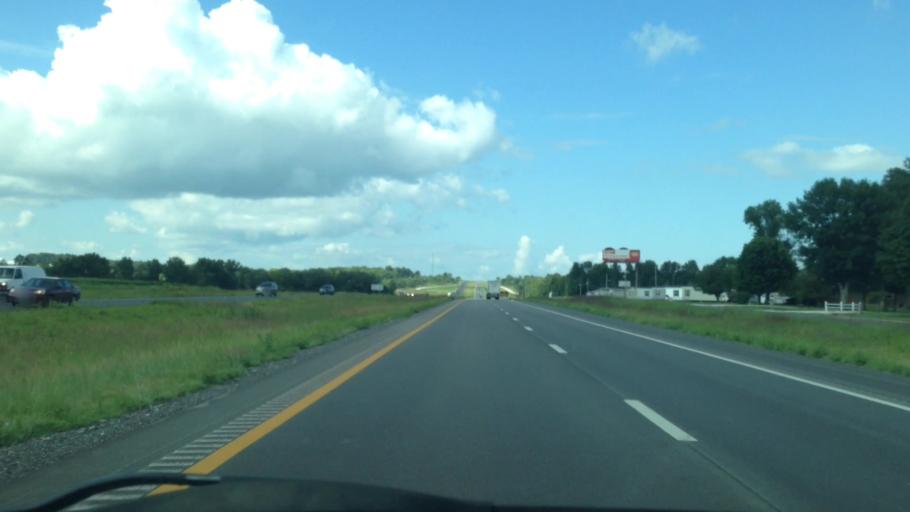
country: US
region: Illinois
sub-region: Adams County
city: Quincy
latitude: 39.9970
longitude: -91.5266
